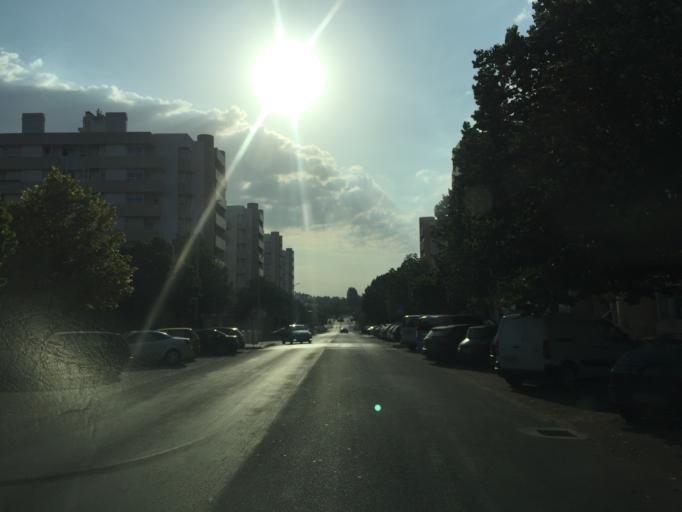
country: PT
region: Santarem
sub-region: Torres Novas
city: Torres Novas
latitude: 39.4732
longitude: -8.5421
